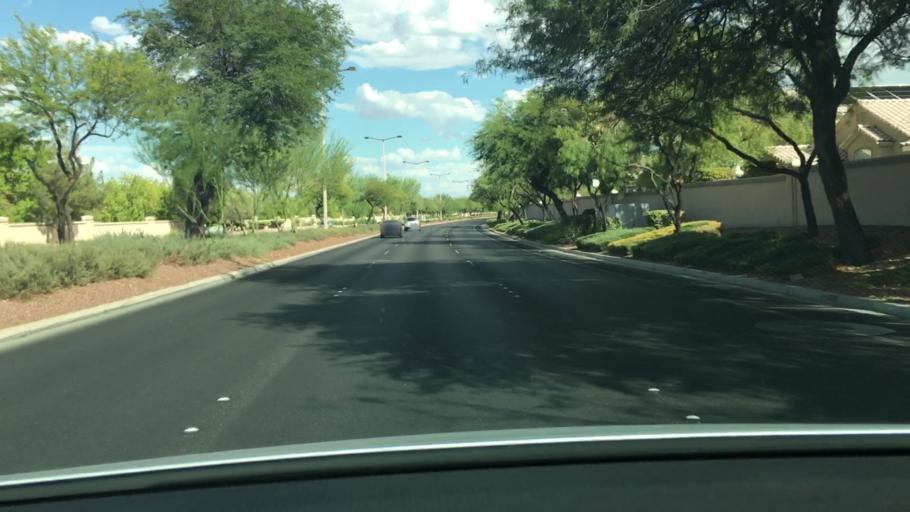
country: US
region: Nevada
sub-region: Clark County
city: Summerlin South
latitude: 36.2050
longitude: -115.2927
